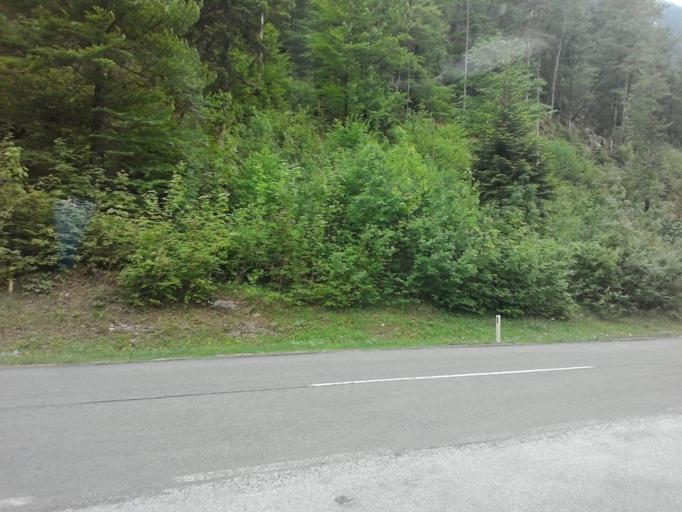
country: AT
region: Styria
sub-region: Politischer Bezirk Liezen
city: Wildalpen
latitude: 47.6837
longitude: 14.9243
